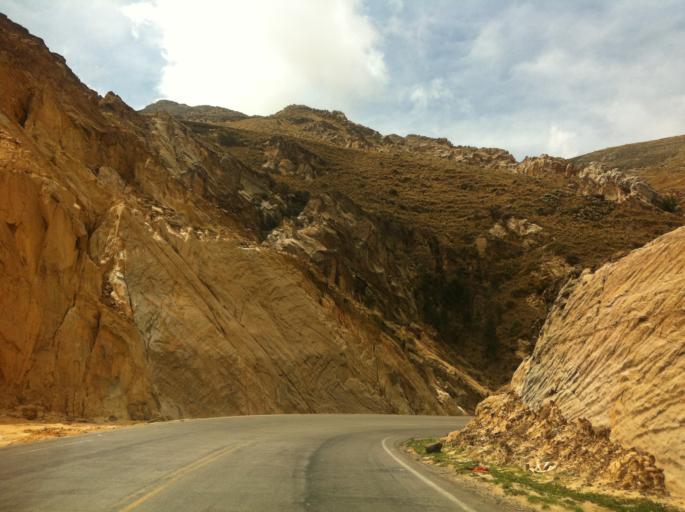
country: BO
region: Cochabamba
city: Irpa Irpa
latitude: -17.7001
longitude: -66.4932
